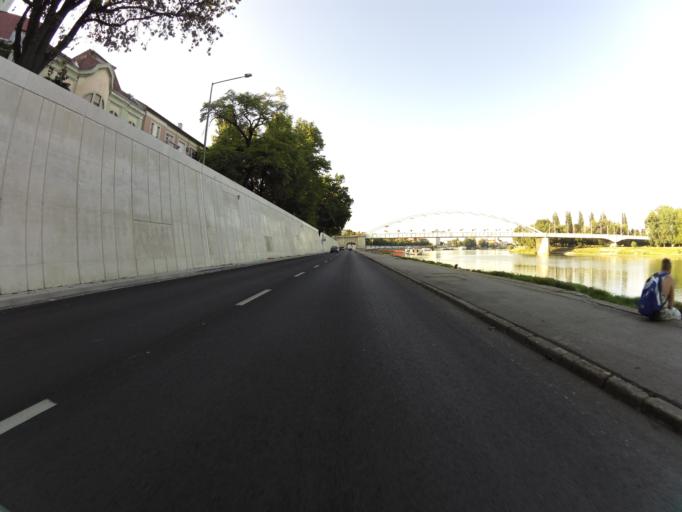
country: HU
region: Csongrad
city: Szeged
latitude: 46.2488
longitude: 20.1515
